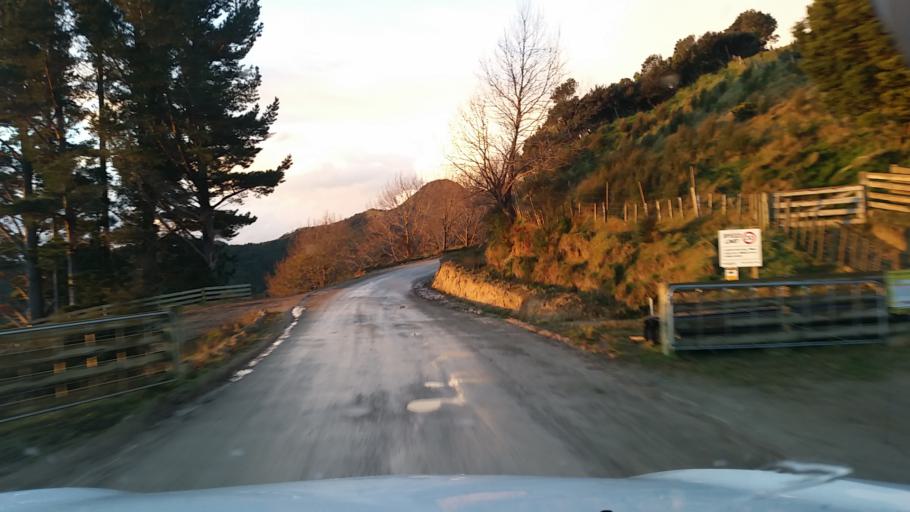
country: NZ
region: Manawatu-Wanganui
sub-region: Wanganui District
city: Wanganui
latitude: -39.7663
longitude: 174.8722
